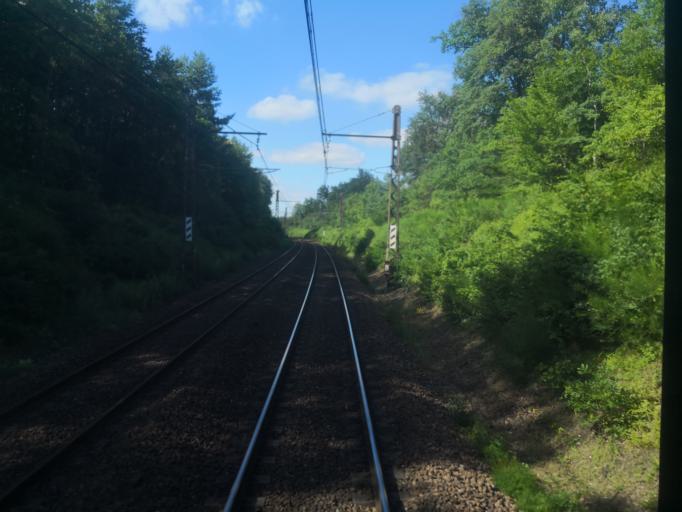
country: FR
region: Ile-de-France
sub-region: Departement de Seine-et-Marne
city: Samoreau
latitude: 48.4307
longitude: 2.7378
